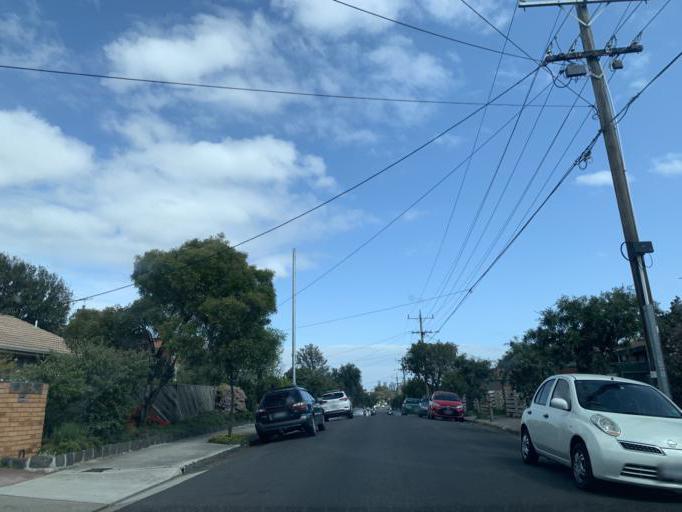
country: AU
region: Victoria
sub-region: Moreland
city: Coburg
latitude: -37.7430
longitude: 144.9716
